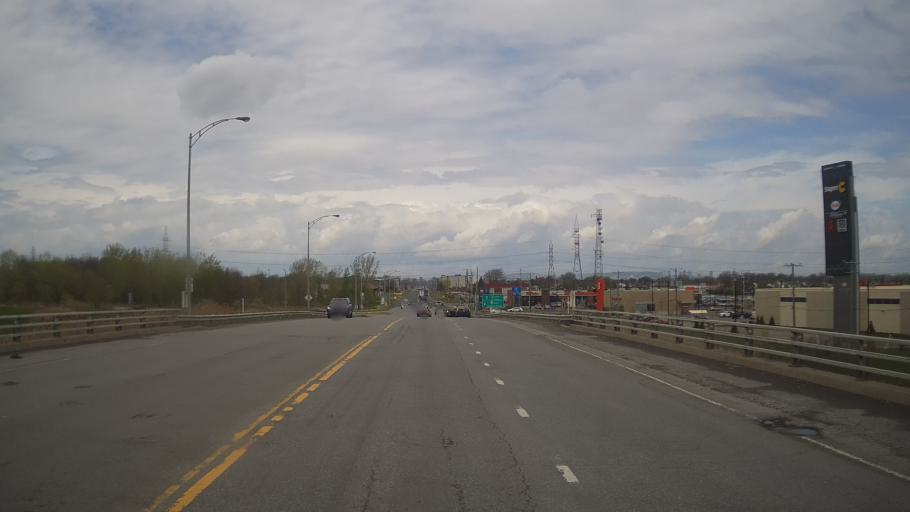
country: CA
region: Quebec
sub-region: Monteregie
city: La Prairie
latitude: 45.4036
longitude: -73.4613
